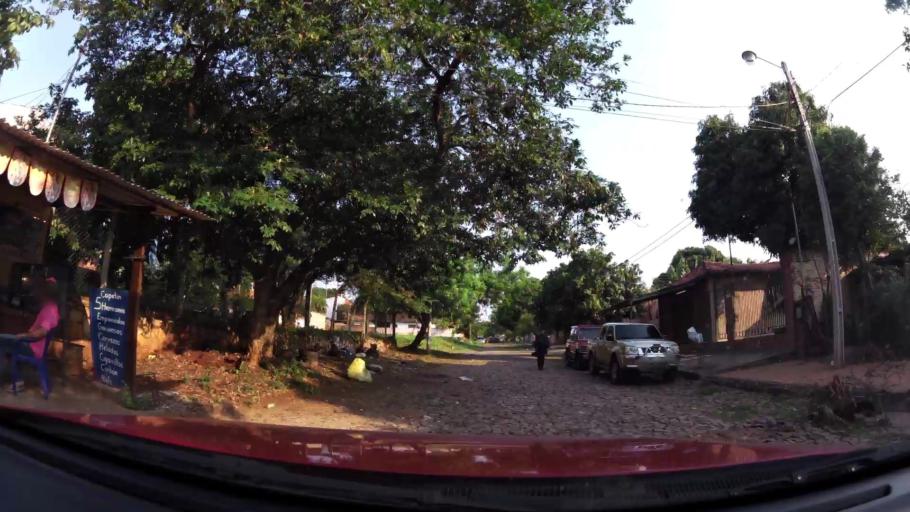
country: PY
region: Central
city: Lambare
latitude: -25.3434
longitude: -57.6004
